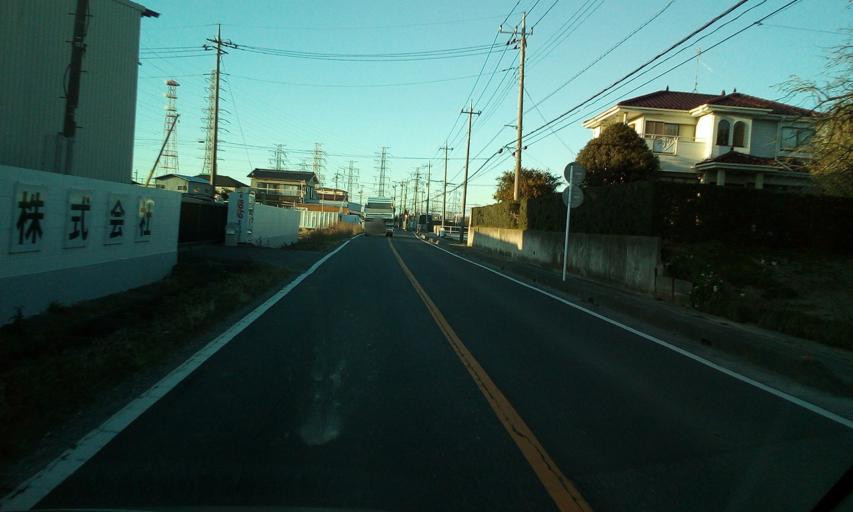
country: JP
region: Chiba
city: Nagareyama
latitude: 35.8651
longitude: 139.8737
